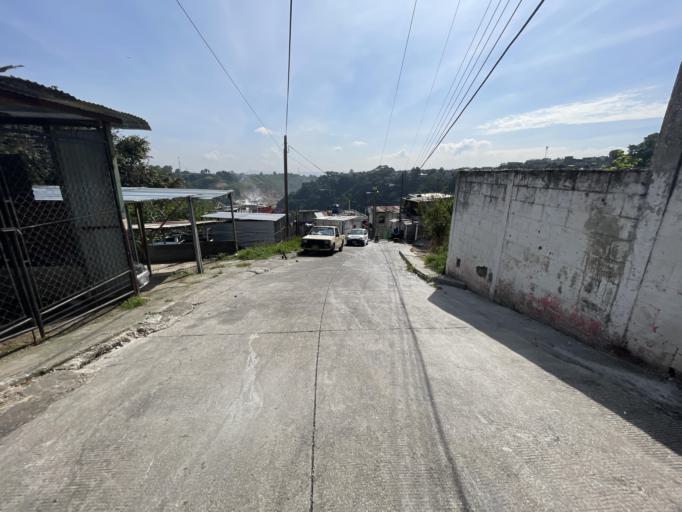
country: GT
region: Guatemala
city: Mixco
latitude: 14.6801
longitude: -90.5765
